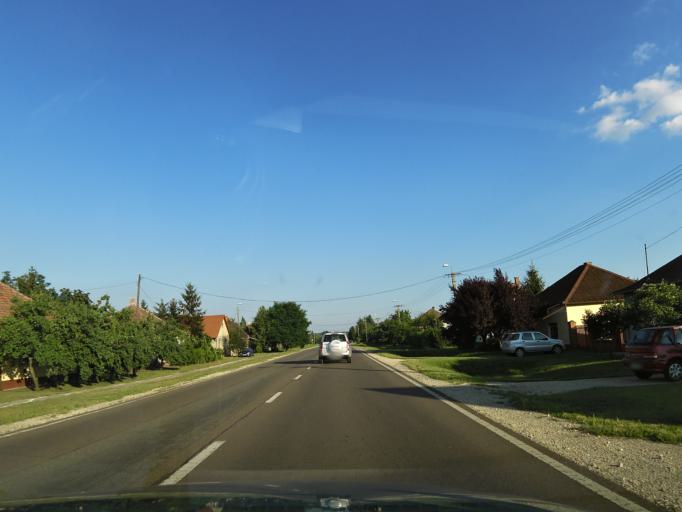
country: HU
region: Jasz-Nagykun-Szolnok
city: Rakocziujfalu
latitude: 47.0564
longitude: 20.2647
